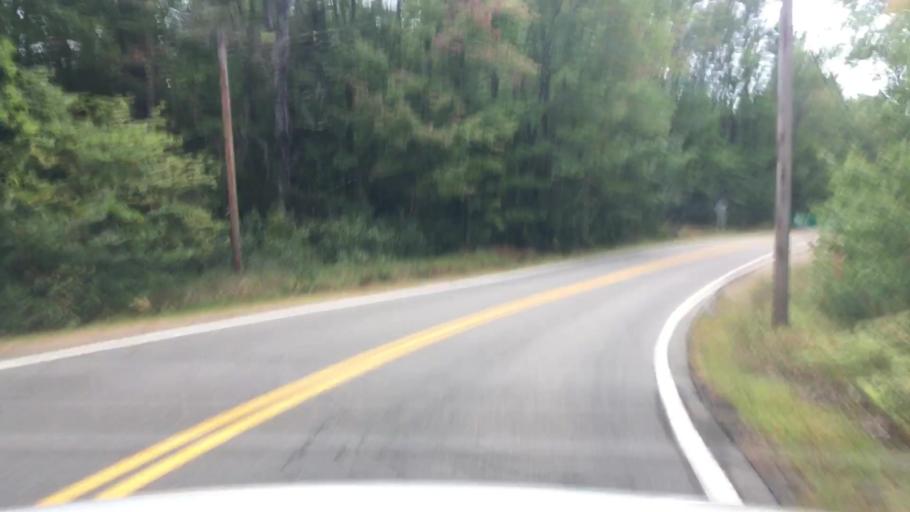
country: US
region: New Hampshire
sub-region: Carroll County
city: Effingham
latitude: 43.7331
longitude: -71.0060
